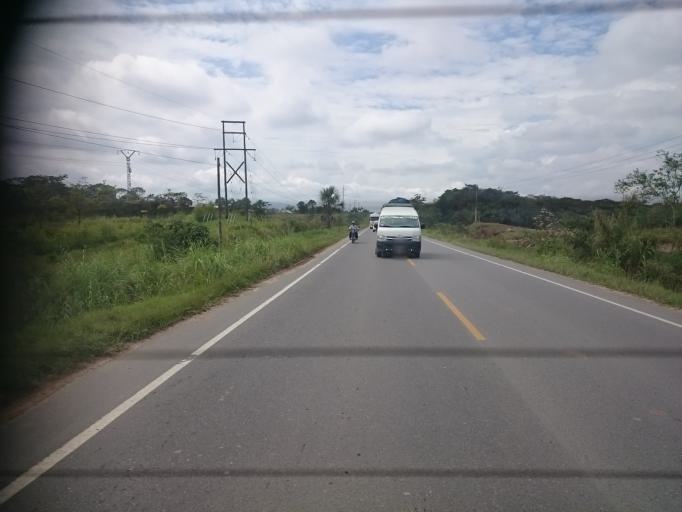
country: PE
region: San Martin
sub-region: Provincia de Rioja
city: Posic
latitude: -6.0276
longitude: -77.2138
